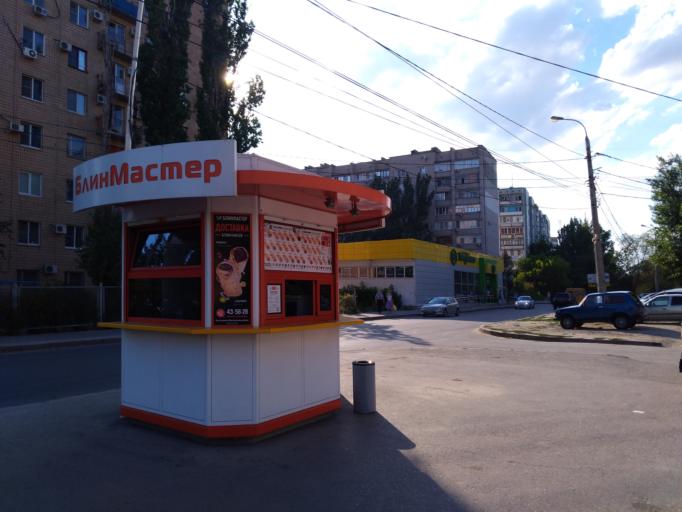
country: RU
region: Volgograd
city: Volgograd
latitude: 48.7188
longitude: 44.5161
